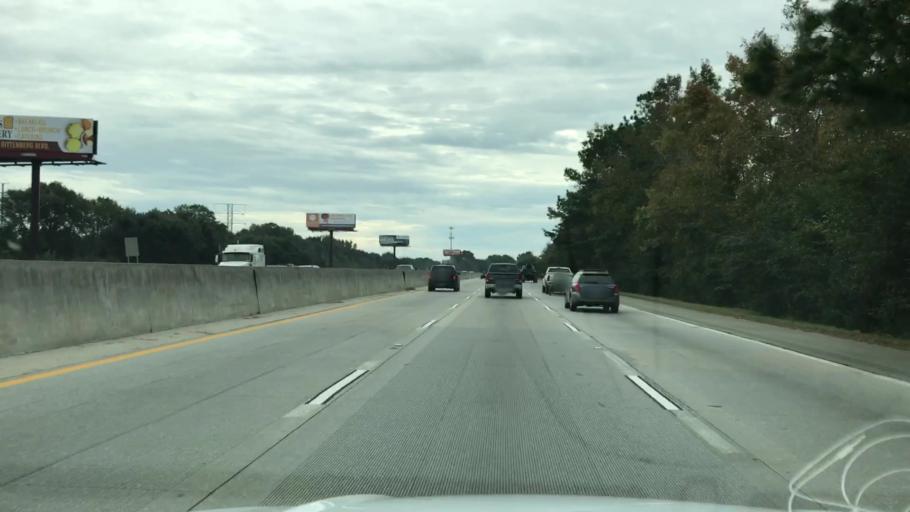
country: US
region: South Carolina
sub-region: Charleston County
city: North Charleston
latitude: 32.8601
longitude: -79.9934
